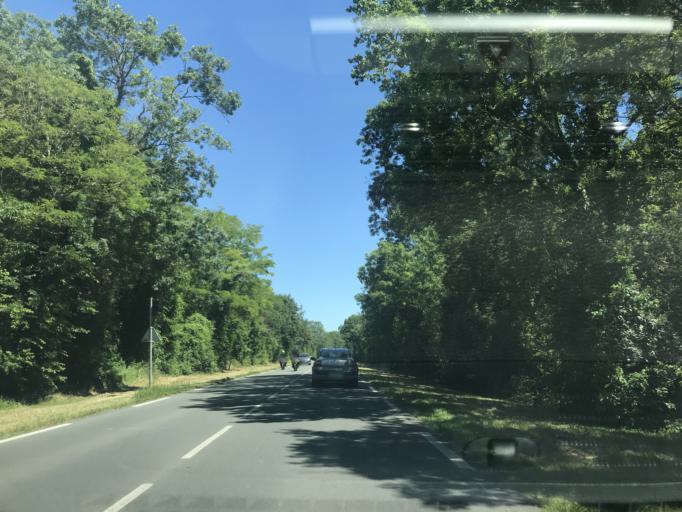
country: FR
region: Poitou-Charentes
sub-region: Departement de la Charente-Maritime
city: Meschers-sur-Gironde
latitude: 45.5642
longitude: -0.9510
